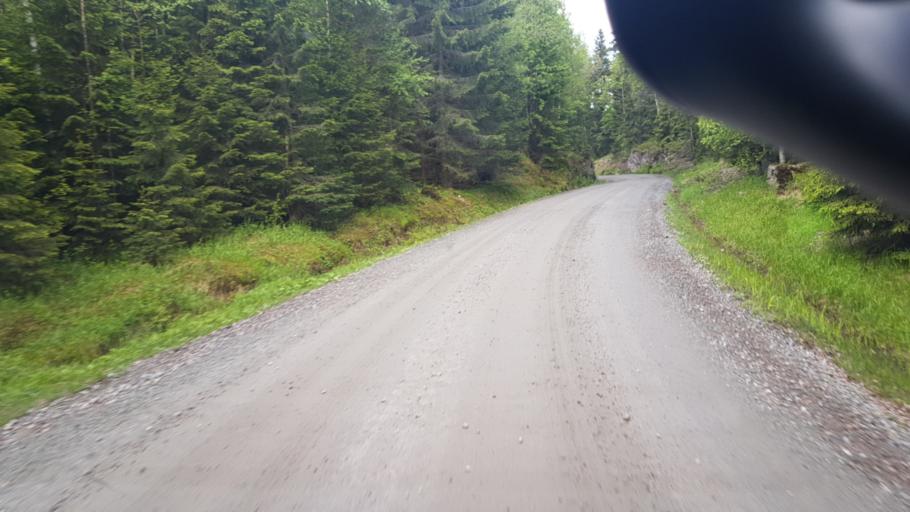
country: NO
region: Ostfold
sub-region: Romskog
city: Romskog
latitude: 59.7142
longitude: 11.9857
